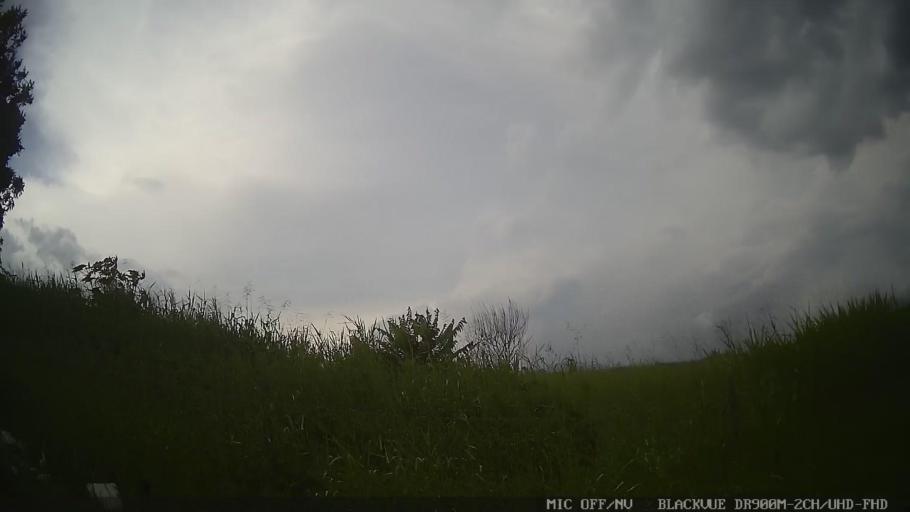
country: BR
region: Sao Paulo
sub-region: Itaquaquecetuba
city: Itaquaquecetuba
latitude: -23.4666
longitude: -46.3126
